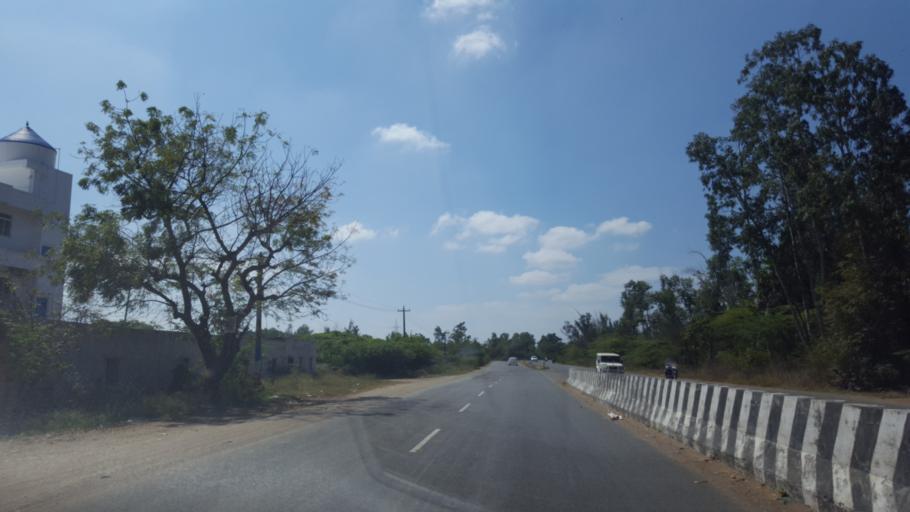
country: IN
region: Tamil Nadu
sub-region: Kancheepuram
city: Mamallapuram
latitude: 12.7013
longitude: 80.1833
